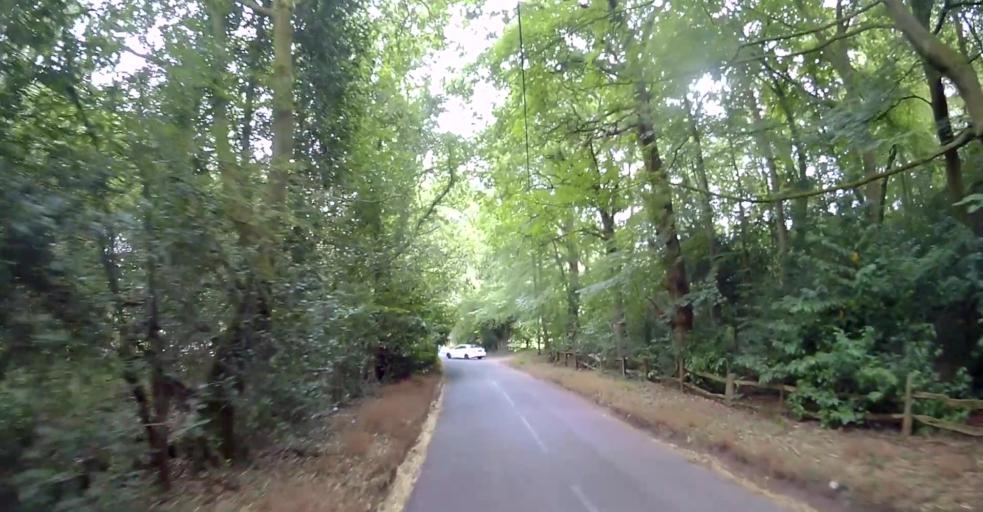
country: GB
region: England
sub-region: Surrey
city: Hale
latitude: 51.2128
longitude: -0.7762
